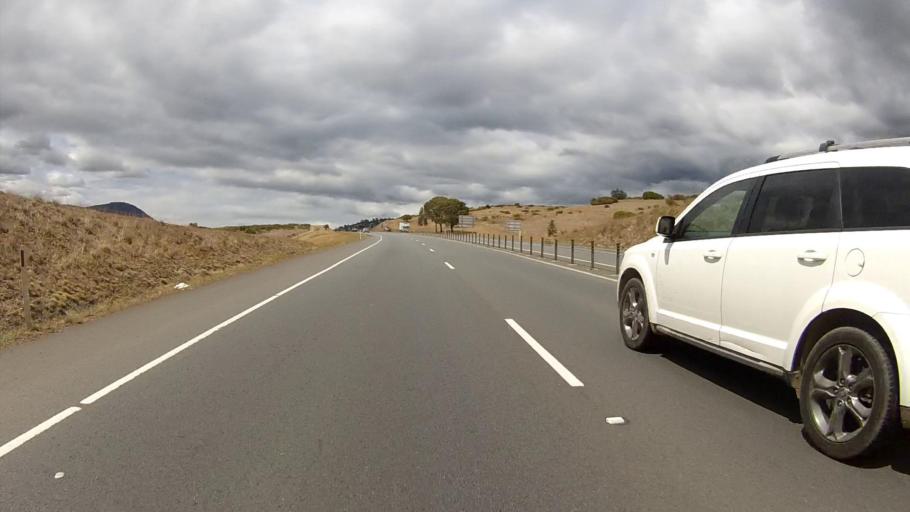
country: AU
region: Tasmania
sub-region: Glenorchy
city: Granton
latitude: -42.7575
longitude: 147.2309
